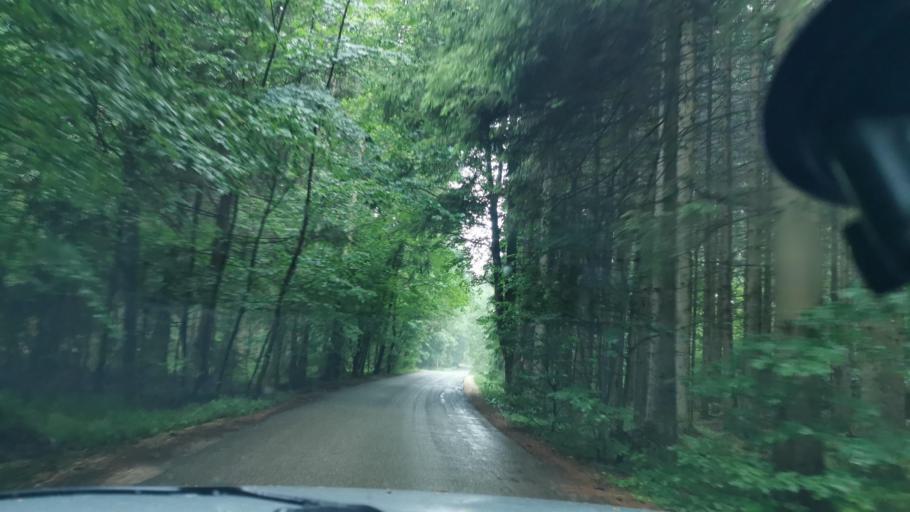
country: DE
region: Baden-Wuerttemberg
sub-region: Regierungsbezirk Stuttgart
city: Bohmenkirch
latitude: 48.7267
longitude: 9.9423
